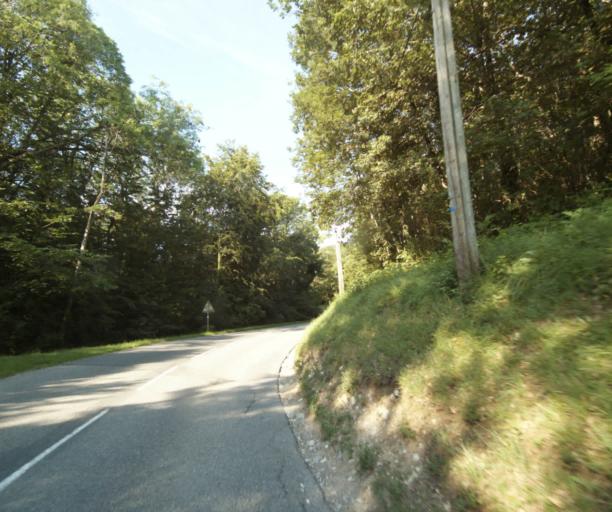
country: FR
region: Rhone-Alpes
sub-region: Departement de la Haute-Savoie
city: Armoy
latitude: 46.3589
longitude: 6.5153
